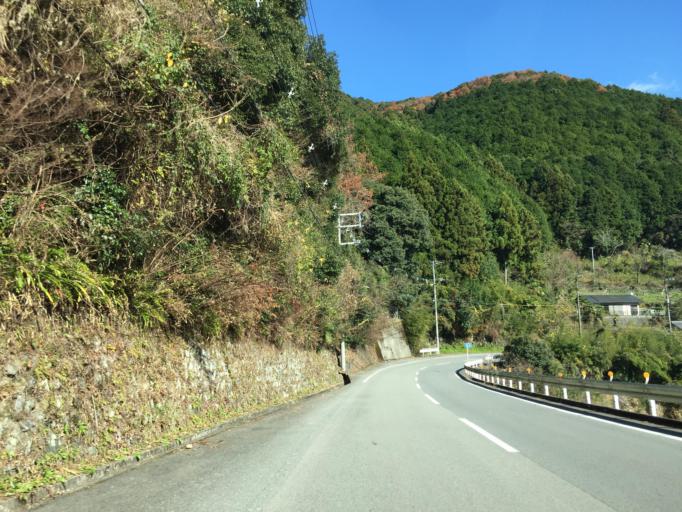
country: JP
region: Wakayama
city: Iwade
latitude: 34.1401
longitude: 135.4095
